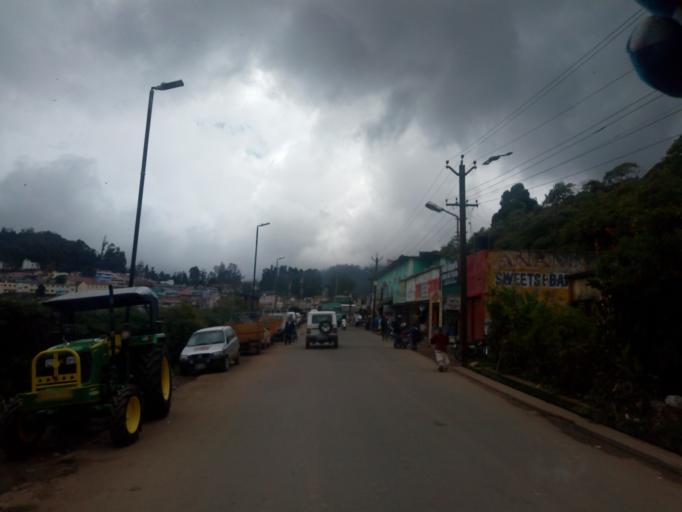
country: IN
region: Tamil Nadu
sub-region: Nilgiri
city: Ooty
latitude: 11.4038
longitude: 76.7035
